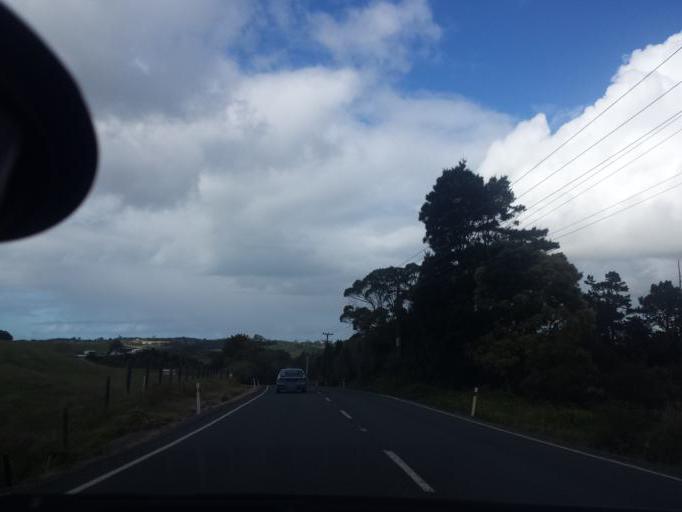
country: NZ
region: Auckland
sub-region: Auckland
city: Warkworth
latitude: -36.3976
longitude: 174.6834
